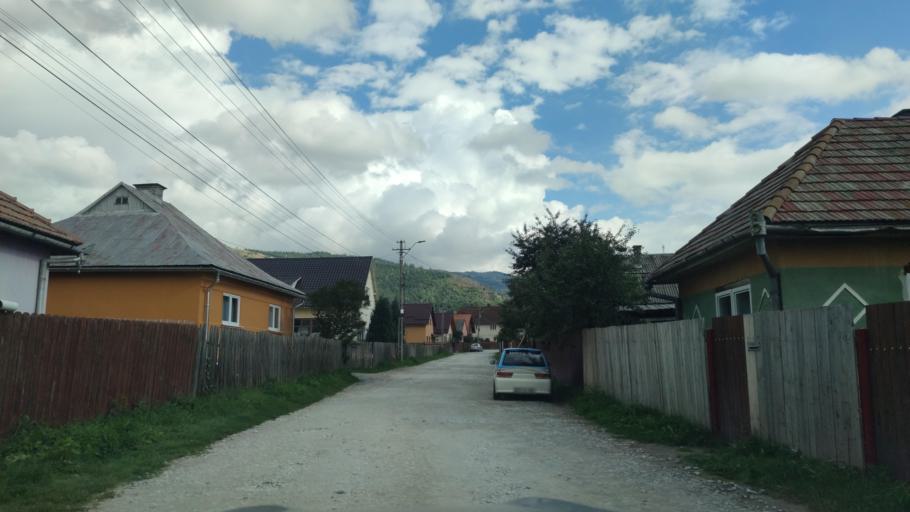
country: RO
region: Harghita
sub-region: Municipiul Gheorgheni
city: Gheorgheni
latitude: 46.7263
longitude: 25.6337
